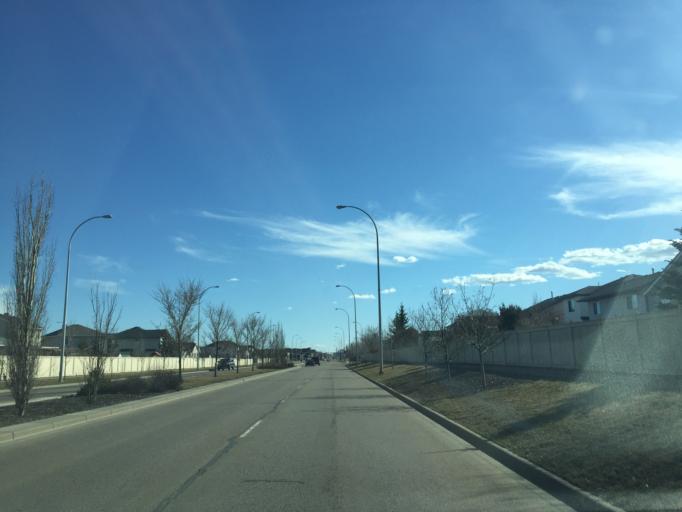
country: CA
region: Alberta
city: Airdrie
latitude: 51.2972
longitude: -114.0254
